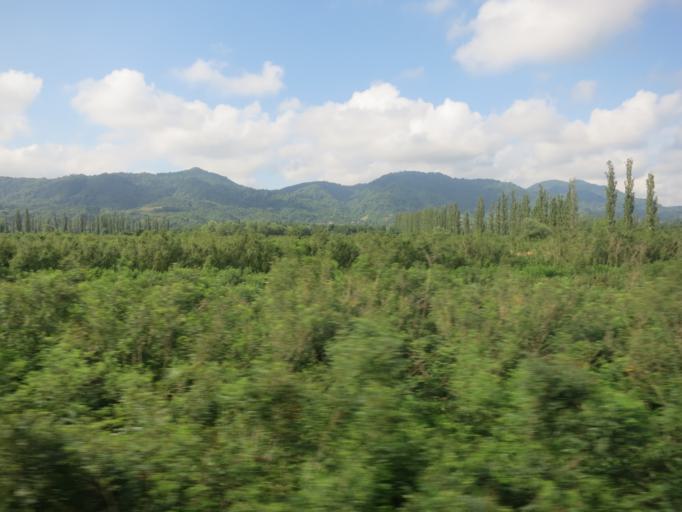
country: GE
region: Guria
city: Lanchkhuti
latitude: 42.0864
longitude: 42.0645
